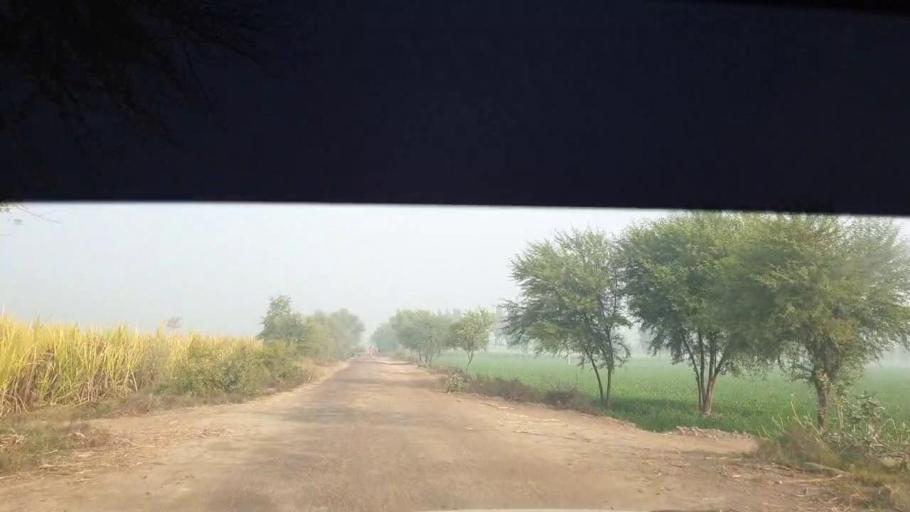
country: PK
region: Sindh
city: Berani
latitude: 25.7865
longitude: 68.7716
